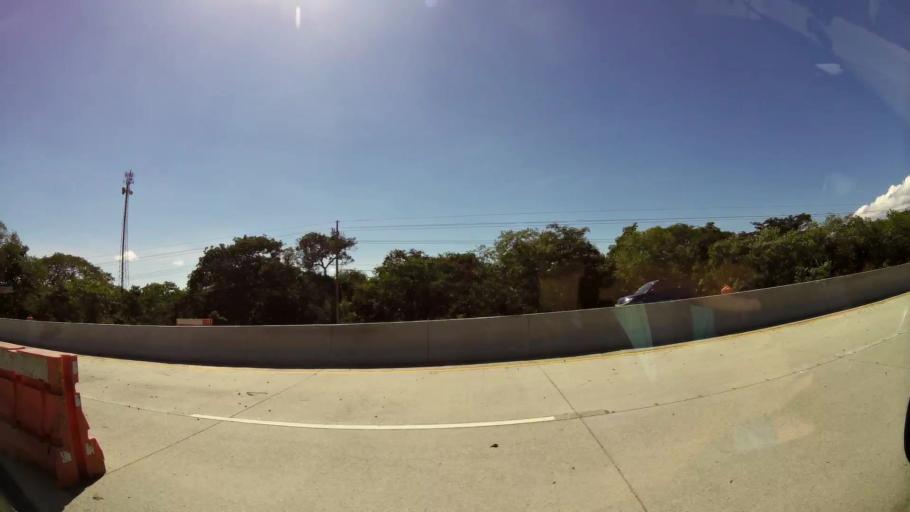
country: CR
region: Guanacaste
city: Liberia
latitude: 10.6223
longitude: -85.4407
